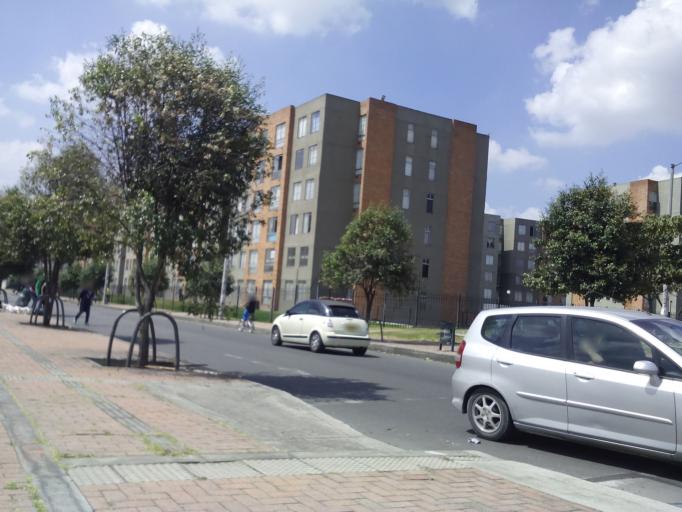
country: CO
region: Bogota D.C.
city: Bogota
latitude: 4.6739
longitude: -74.1345
